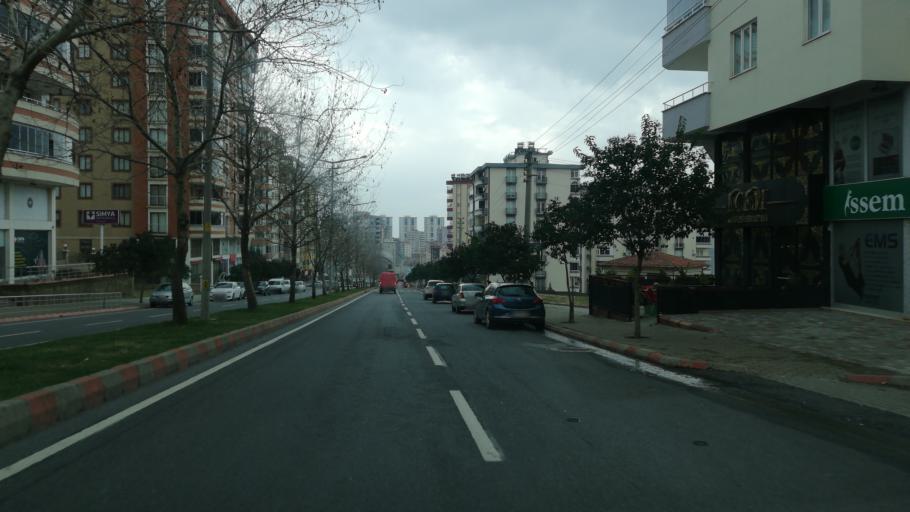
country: TR
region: Kahramanmaras
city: Kahramanmaras
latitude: 37.5858
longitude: 36.8789
